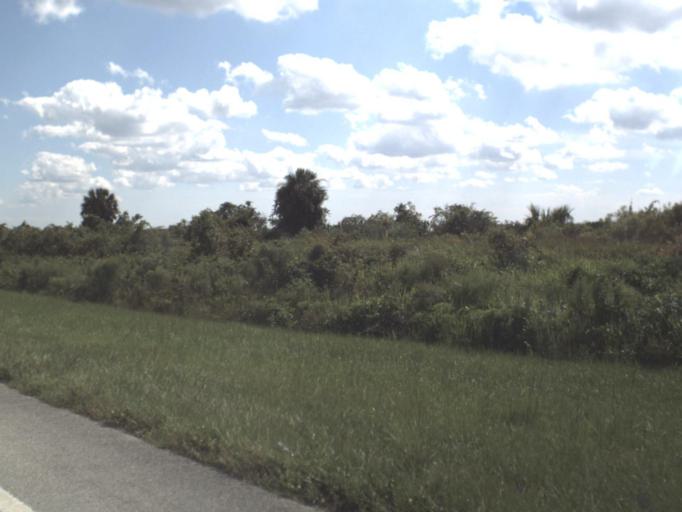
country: US
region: Florida
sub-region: Highlands County
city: Lake Placid
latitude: 27.3943
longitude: -81.1527
